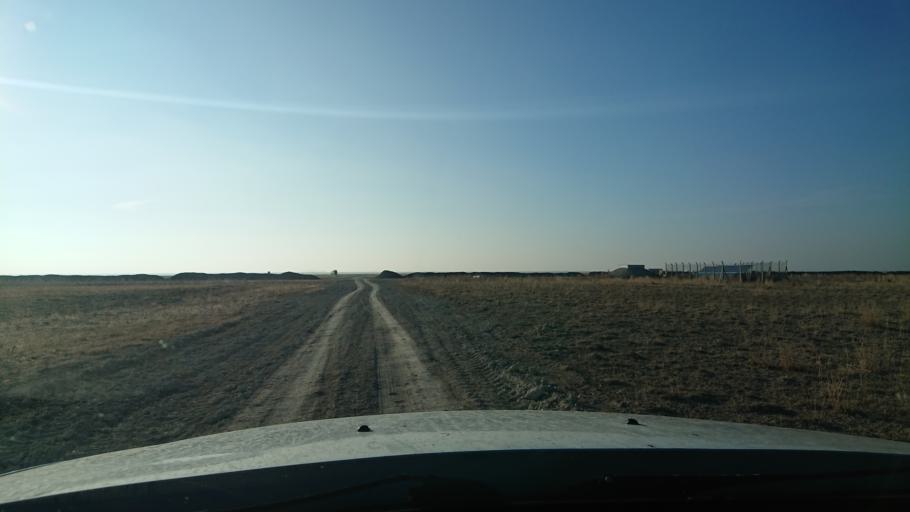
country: TR
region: Aksaray
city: Eskil
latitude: 38.3715
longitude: 33.5278
